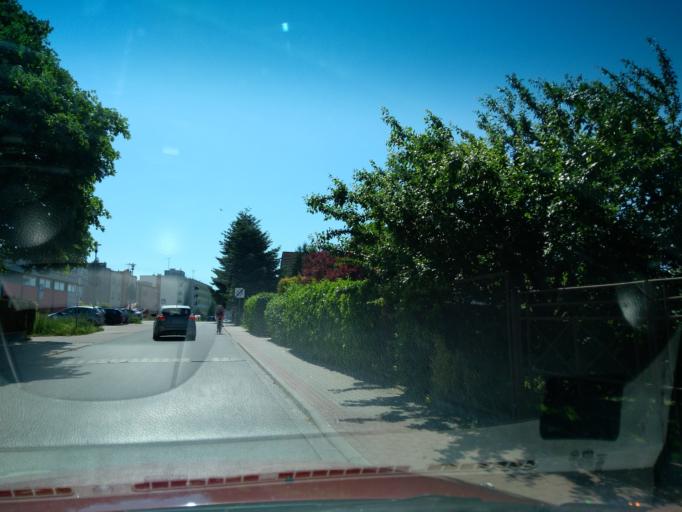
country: PL
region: West Pomeranian Voivodeship
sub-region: Koszalin
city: Koszalin
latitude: 54.2075
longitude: 16.1789
